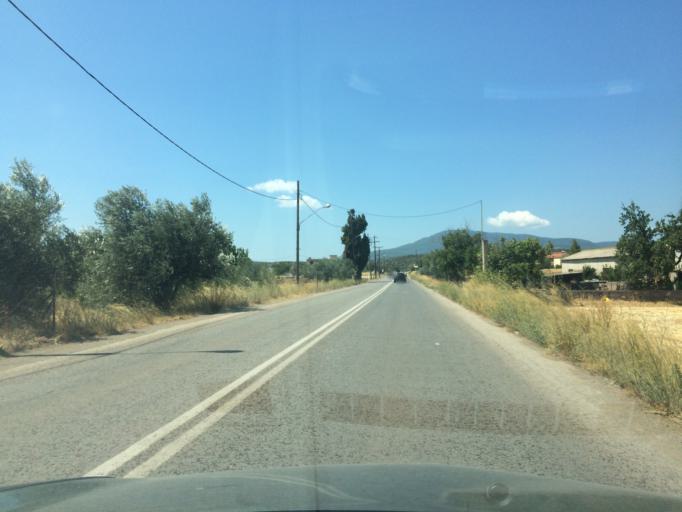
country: GR
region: Central Greece
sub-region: Nomos Evvoias
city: Psachna
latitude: 38.5775
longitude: 23.6300
